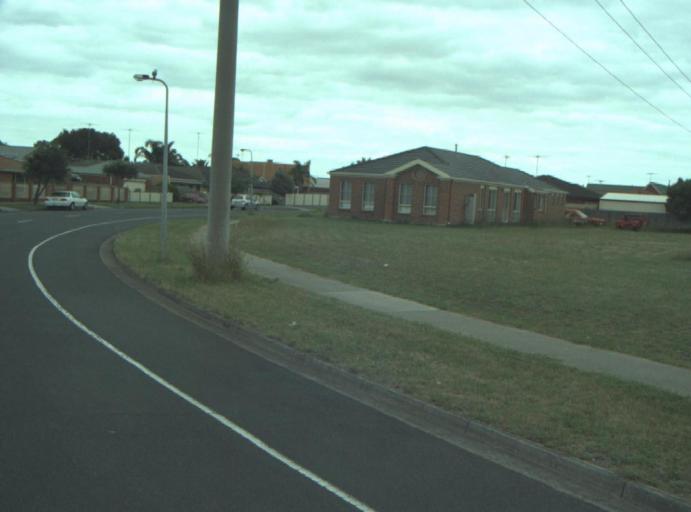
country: AU
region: Victoria
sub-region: Greater Geelong
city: Wandana Heights
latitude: -38.1966
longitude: 144.3278
